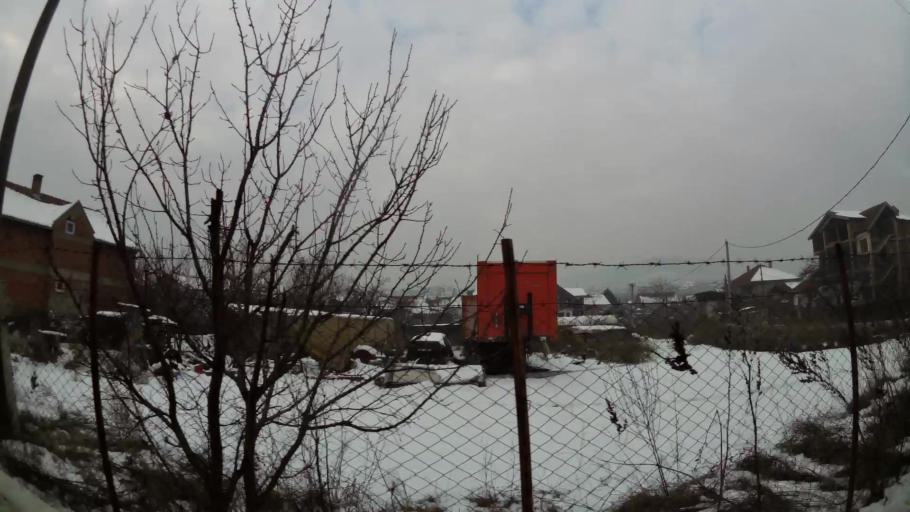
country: MK
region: Saraj
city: Saraj
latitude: 42.0421
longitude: 21.3507
